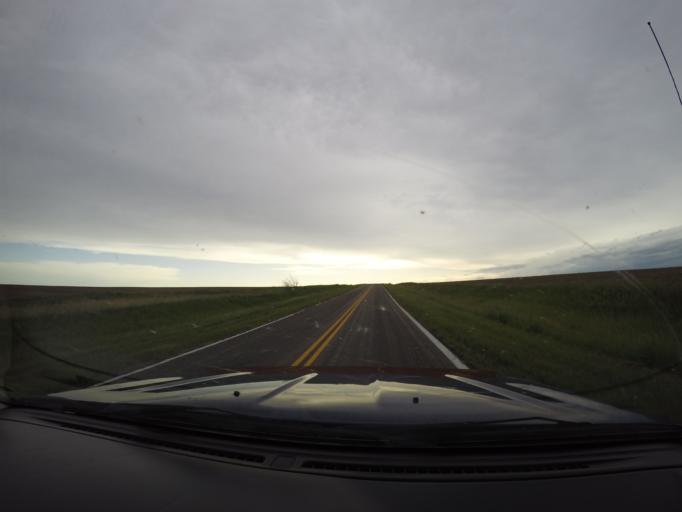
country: US
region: Kansas
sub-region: Smith County
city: Smith Center
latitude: 39.8282
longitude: -98.5658
